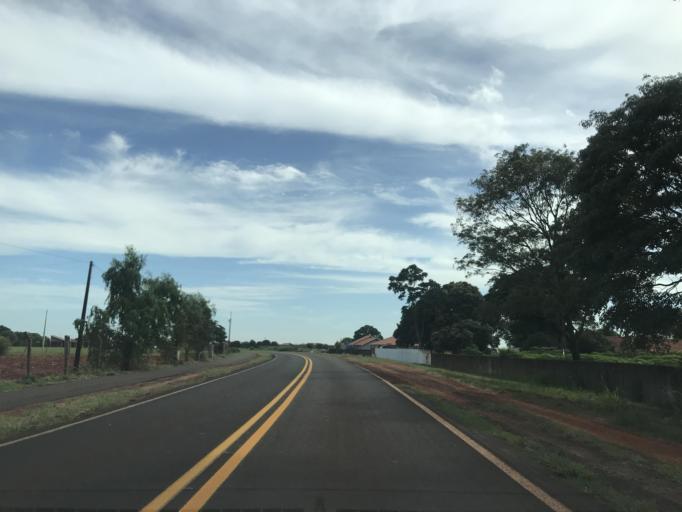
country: BR
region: Parana
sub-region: Terra Rica
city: Terra Rica
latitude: -22.7518
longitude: -52.6256
